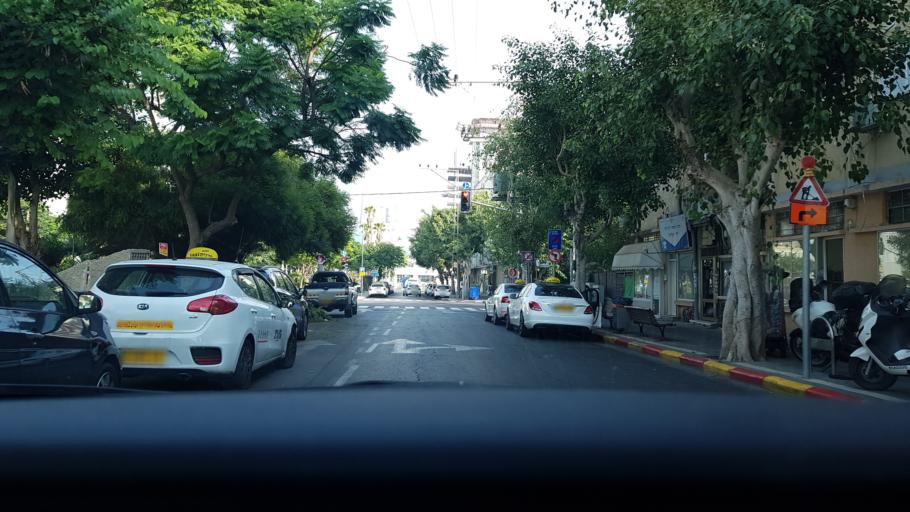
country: IL
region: Tel Aviv
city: Tel Aviv
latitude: 32.0588
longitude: 34.7895
